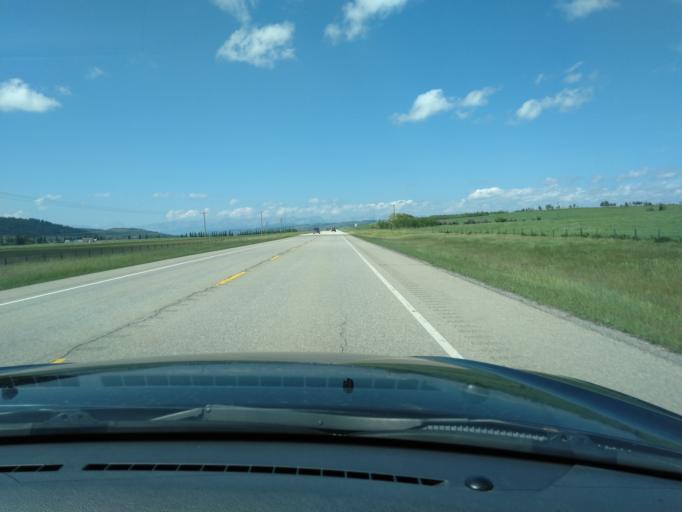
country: CA
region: Alberta
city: Cochrane
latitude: 51.2241
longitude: -114.6566
